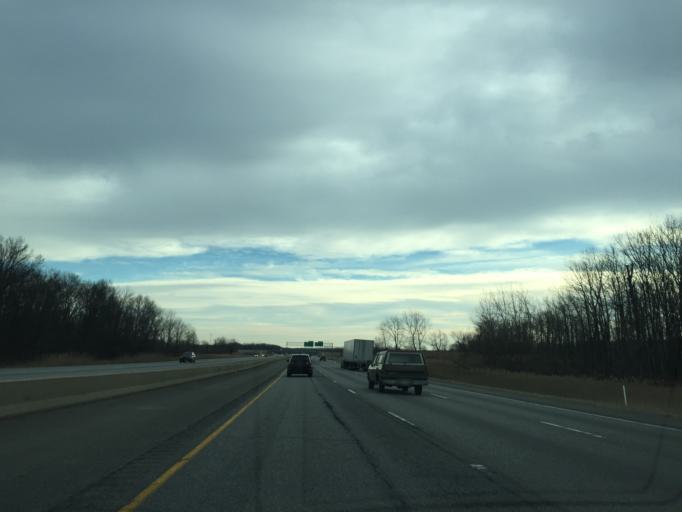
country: US
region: Indiana
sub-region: LaPorte County
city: Michigan City
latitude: 41.6583
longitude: -86.9047
